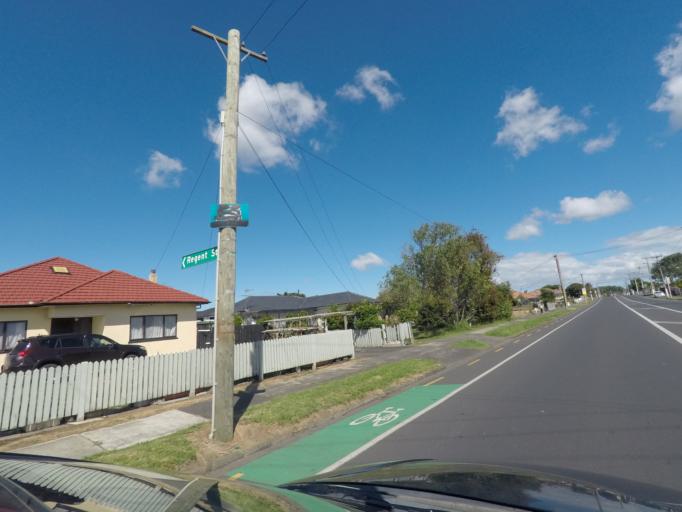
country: NZ
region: Auckland
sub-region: Auckland
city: Manukau City
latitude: -36.9773
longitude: 174.8699
